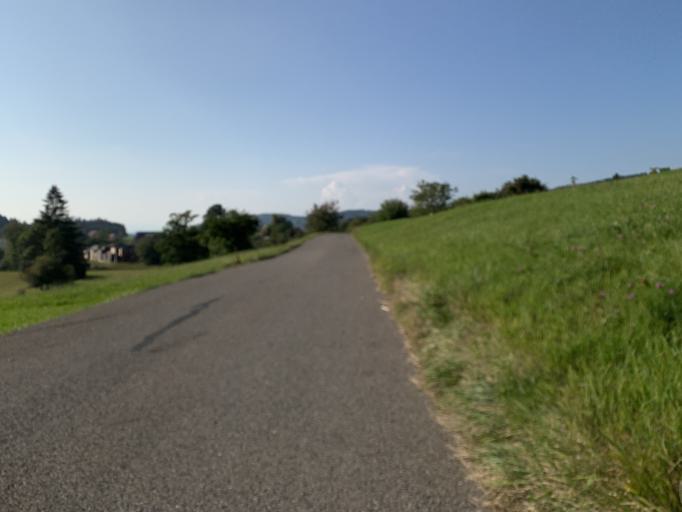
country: CH
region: Zurich
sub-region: Bezirk Hinwil
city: Baretswil
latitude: 47.3241
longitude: 8.8757
